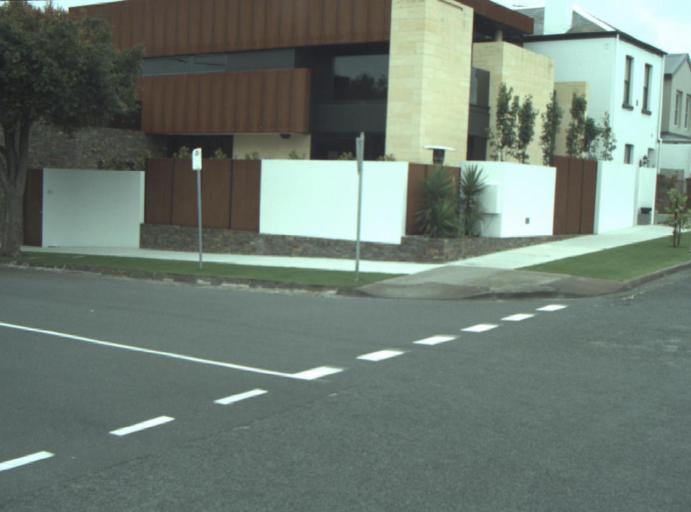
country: AU
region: Victoria
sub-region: Greater Geelong
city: Geelong
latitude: -38.1537
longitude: 144.3549
